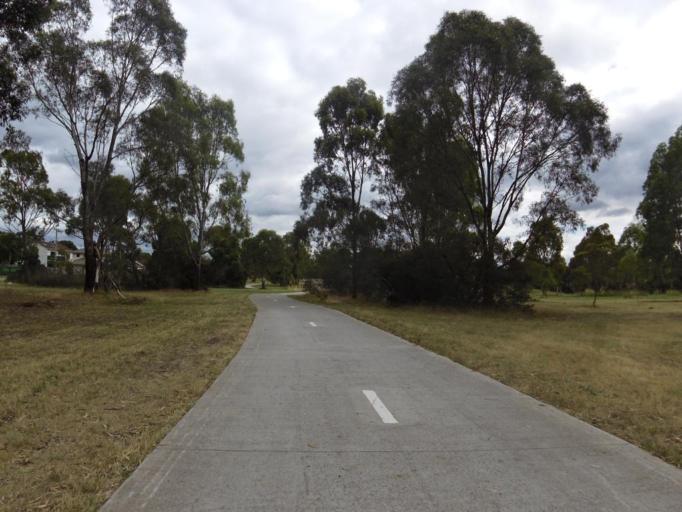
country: AU
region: Victoria
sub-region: Darebin
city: Kingsbury
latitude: -37.7300
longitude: 145.0376
